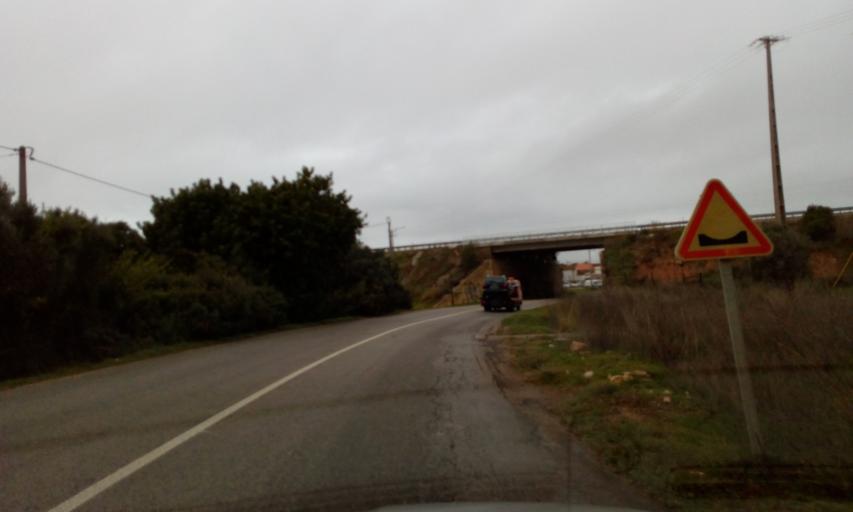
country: PT
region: Faro
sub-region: Albufeira
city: Ferreiras
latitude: 37.1383
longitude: -8.2672
